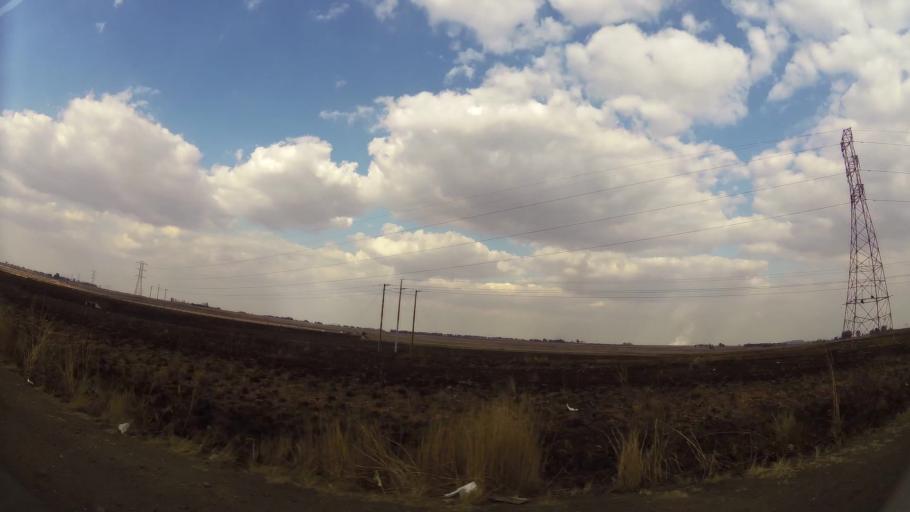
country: ZA
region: Mpumalanga
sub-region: Nkangala District Municipality
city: Delmas
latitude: -26.1758
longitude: 28.6974
